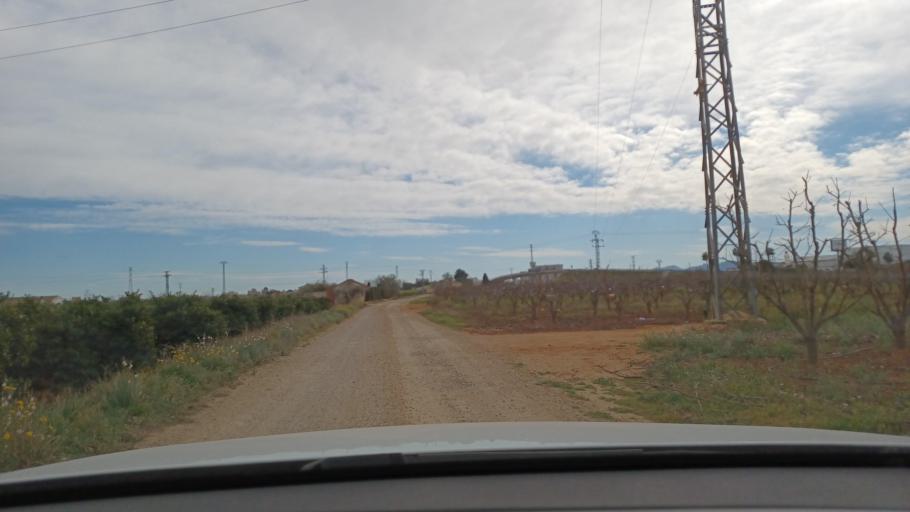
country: ES
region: Valencia
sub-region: Provincia de Valencia
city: Benifaio
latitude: 39.2914
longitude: -0.4428
